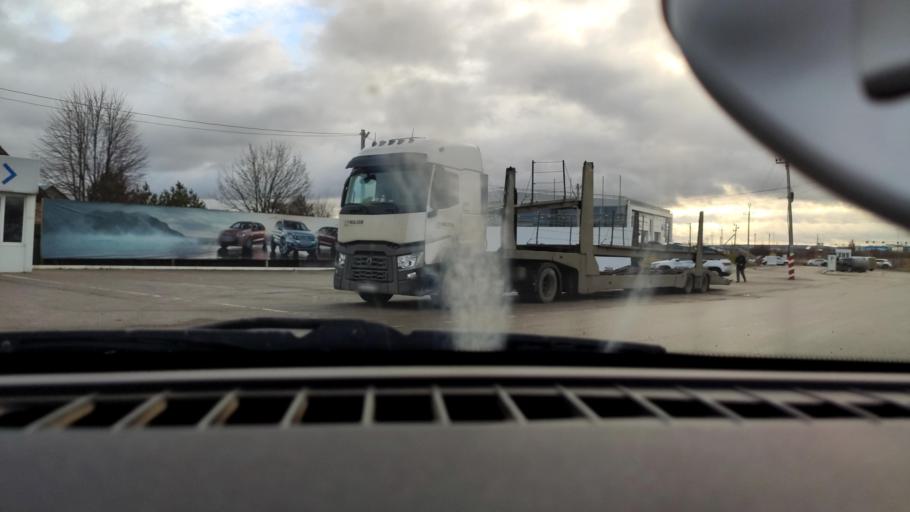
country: RU
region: Perm
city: Kondratovo
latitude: 57.9546
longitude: 56.1250
